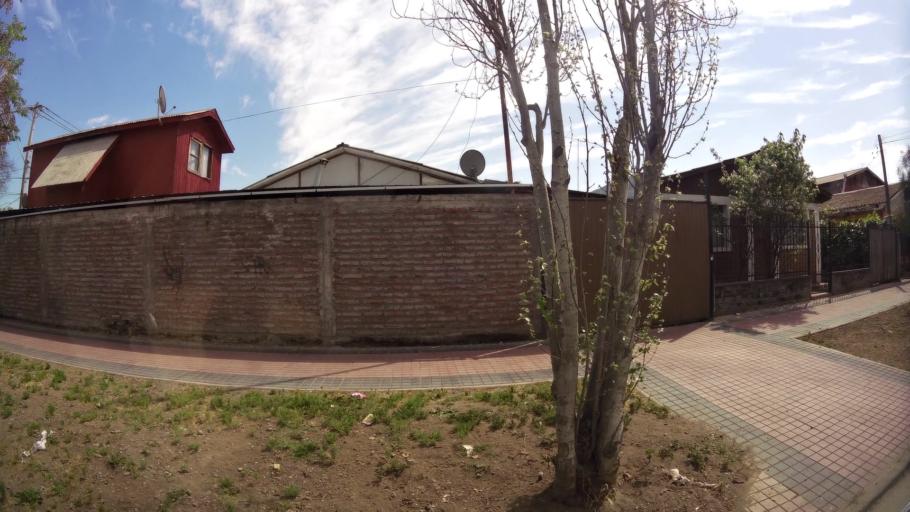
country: CL
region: Santiago Metropolitan
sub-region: Provincia de Talagante
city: Talagante
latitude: -33.6656
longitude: -70.9205
